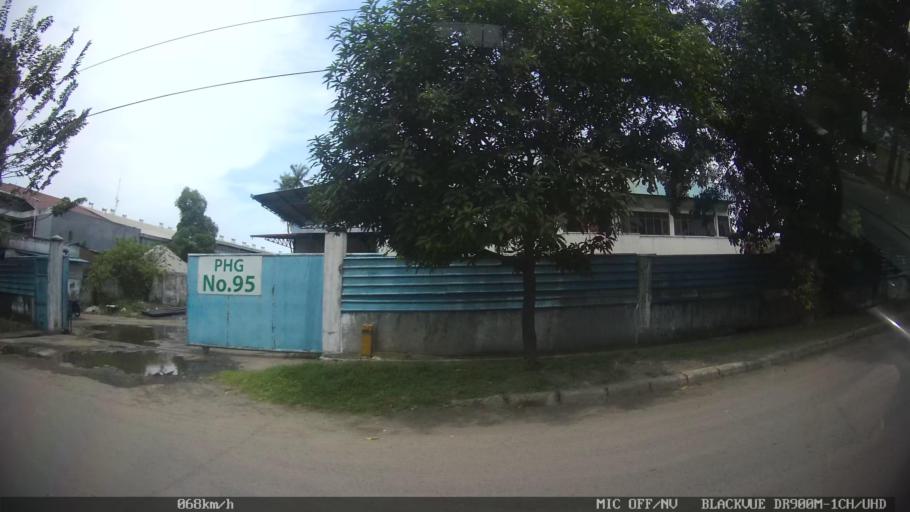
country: ID
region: North Sumatra
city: Labuhan Deli
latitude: 3.6633
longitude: 98.6665
